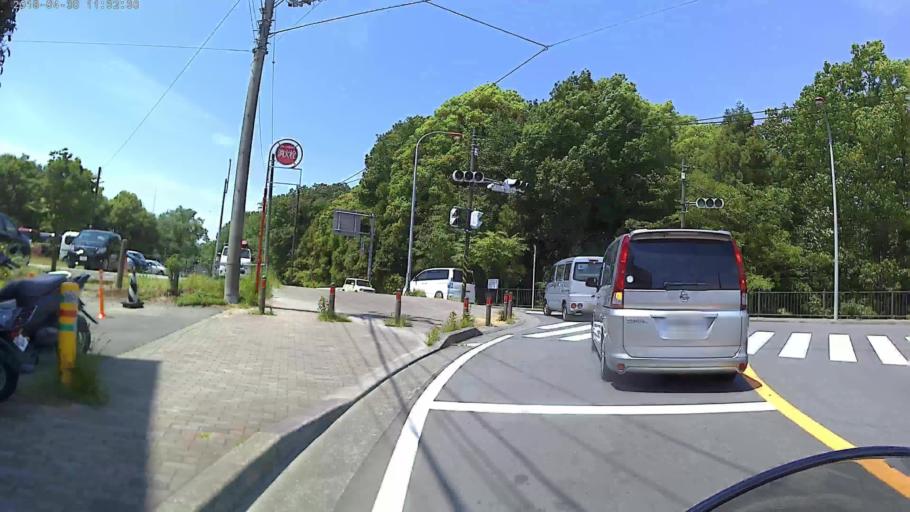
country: JP
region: Kanagawa
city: Zama
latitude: 35.4848
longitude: 139.4066
